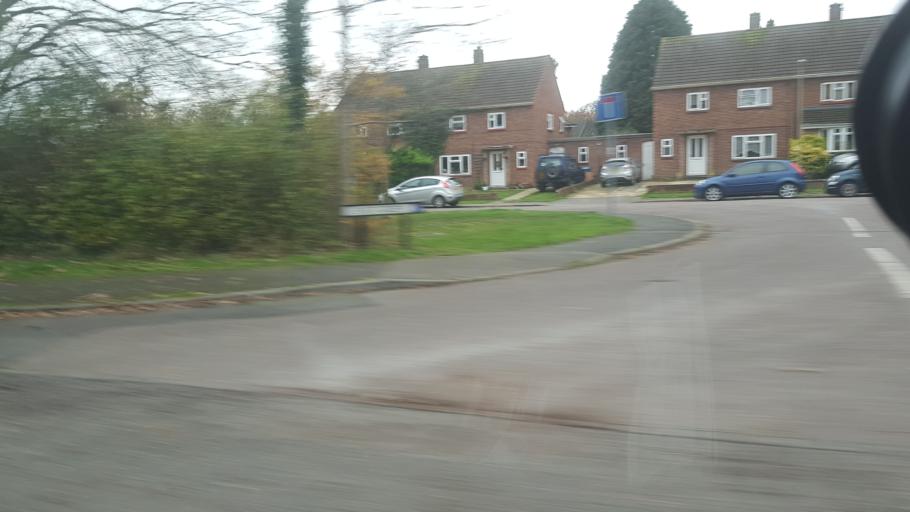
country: GB
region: England
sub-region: Bracknell Forest
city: Sandhurst
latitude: 51.3313
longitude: -0.7933
